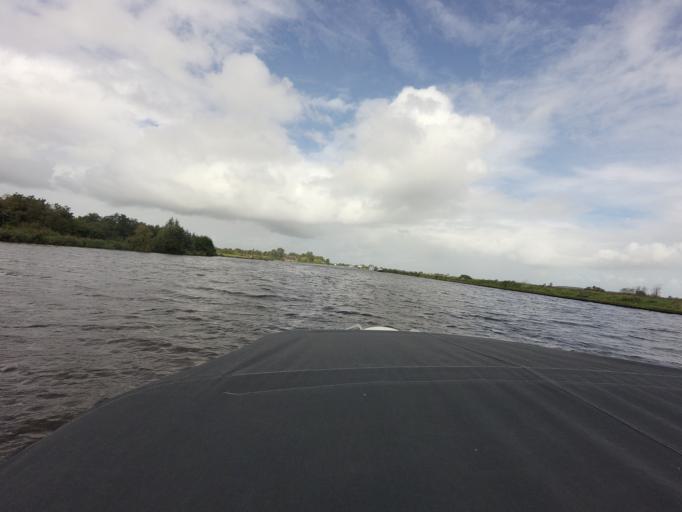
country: NL
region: Friesland
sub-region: Gemeente Boarnsterhim
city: Warten
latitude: 53.1343
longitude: 5.9194
